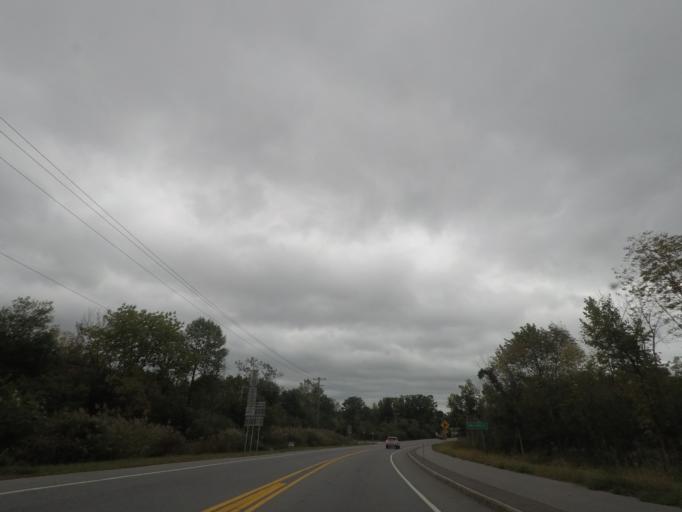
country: US
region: New York
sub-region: Saratoga County
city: Country Knolls
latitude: 42.9484
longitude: -73.7885
